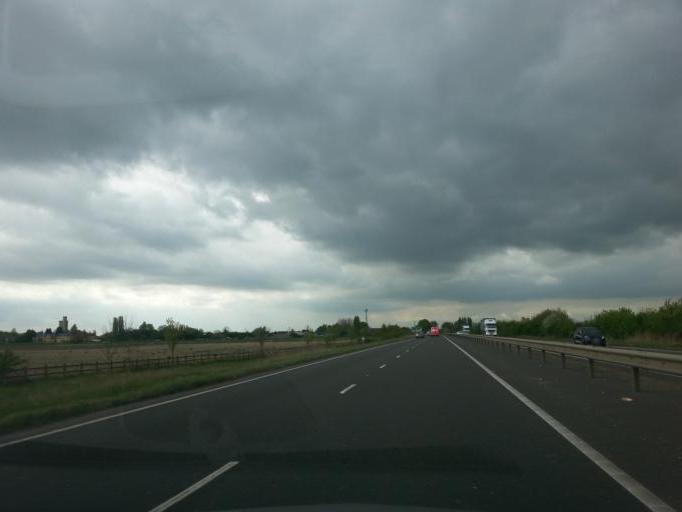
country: GB
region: England
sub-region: Peterborough
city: Thorney
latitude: 52.6260
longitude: -0.0972
